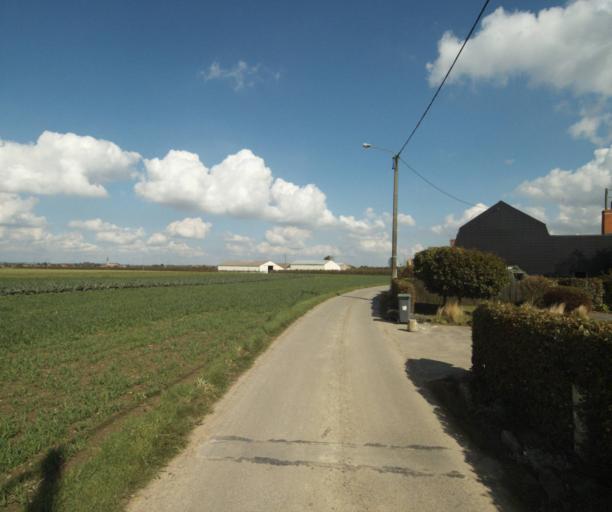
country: FR
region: Nord-Pas-de-Calais
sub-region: Departement du Nord
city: Aubers
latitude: 50.5799
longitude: 2.8259
